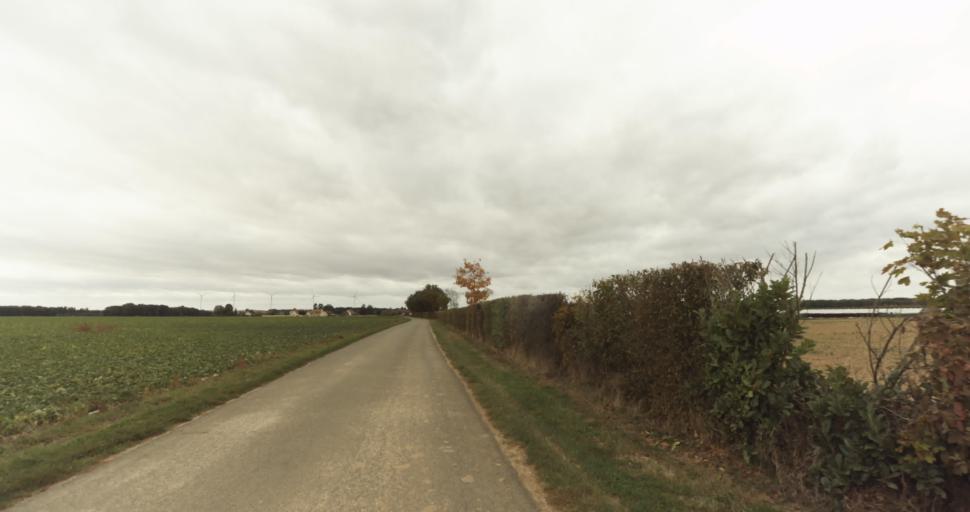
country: FR
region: Centre
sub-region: Departement d'Eure-et-Loir
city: Vernouillet
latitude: 48.6779
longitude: 1.3716
